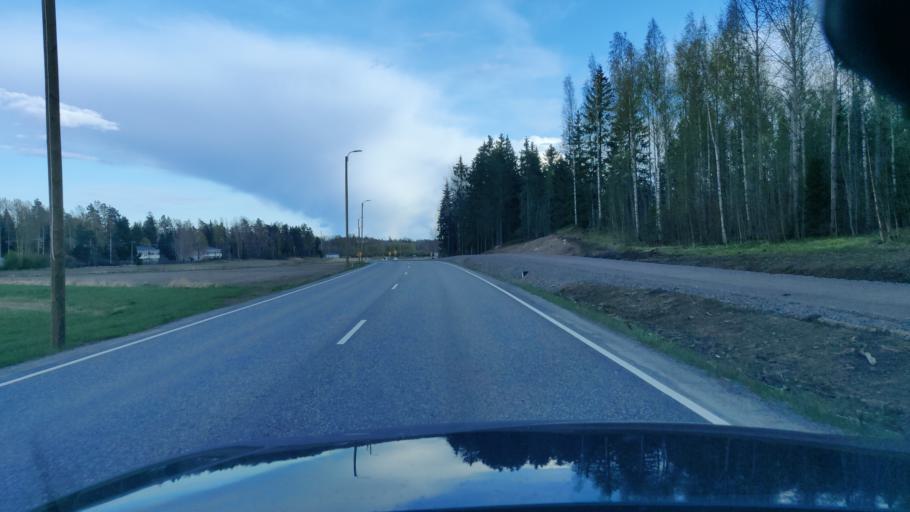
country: FI
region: Uusimaa
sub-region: Helsinki
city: Jaervenpaeae
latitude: 60.4740
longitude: 25.0671
